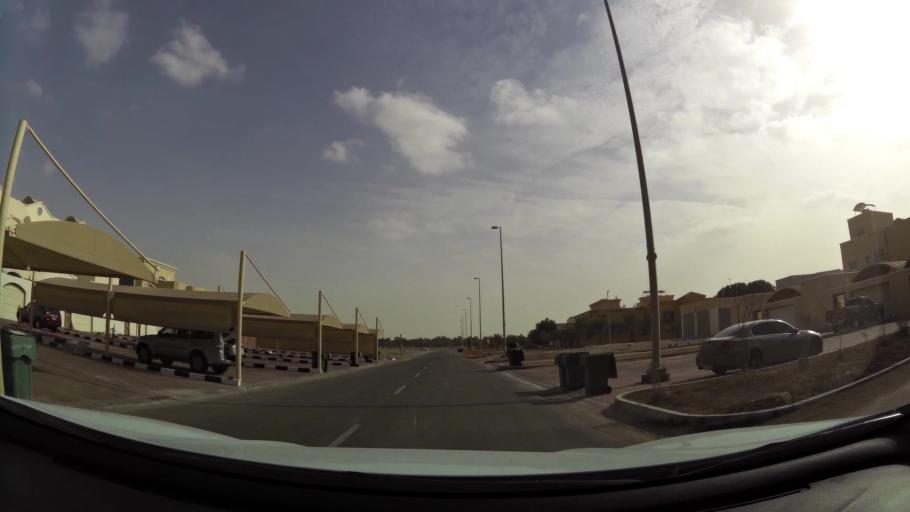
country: AE
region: Abu Dhabi
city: Abu Dhabi
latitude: 24.4072
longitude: 54.5965
